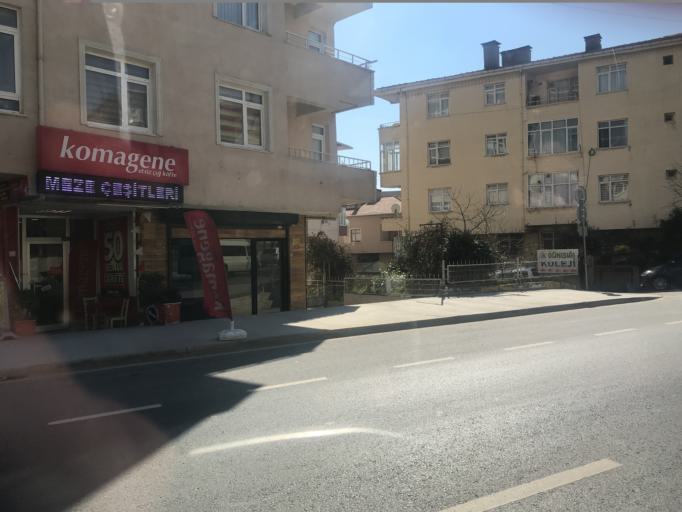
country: TR
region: Istanbul
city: Pendik
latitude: 40.8989
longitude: 29.2552
